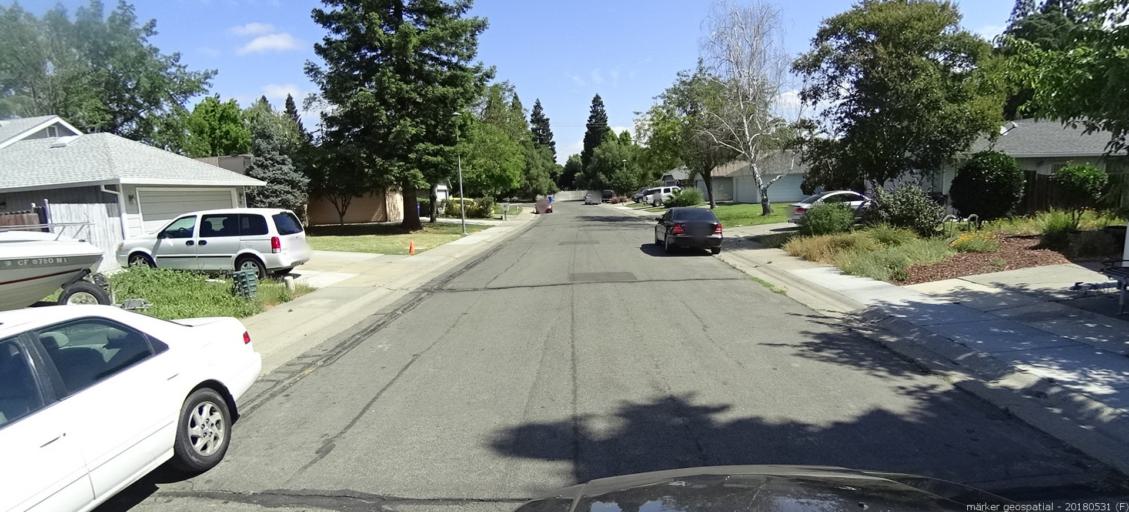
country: US
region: California
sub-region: Sacramento County
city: Sacramento
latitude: 38.6265
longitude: -121.5042
